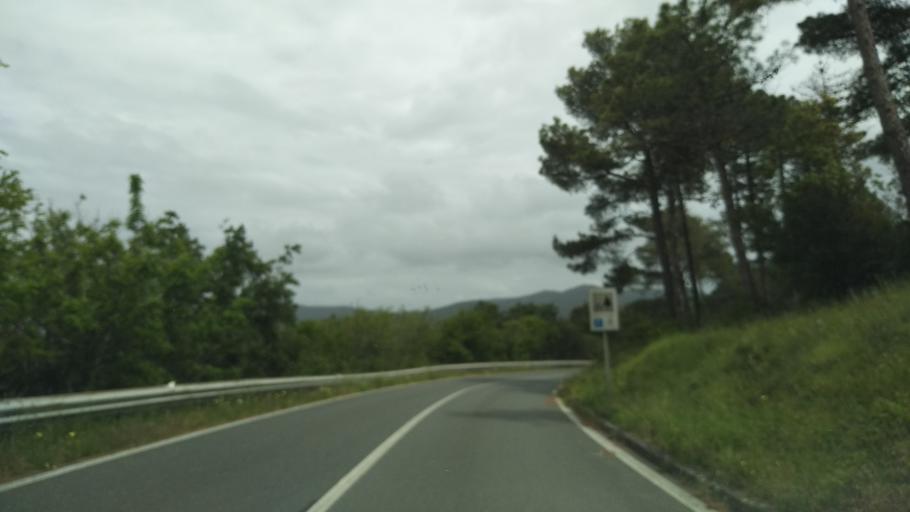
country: IT
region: Tuscany
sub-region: Provincia di Livorno
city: Quercianella
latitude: 43.4933
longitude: 10.3587
